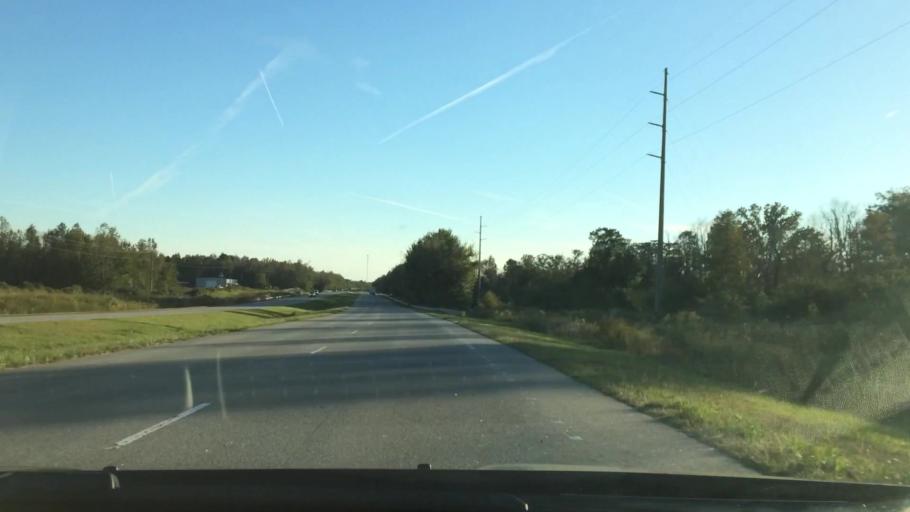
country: US
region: North Carolina
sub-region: Pitt County
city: Grifton
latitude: 35.3919
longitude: -77.4460
